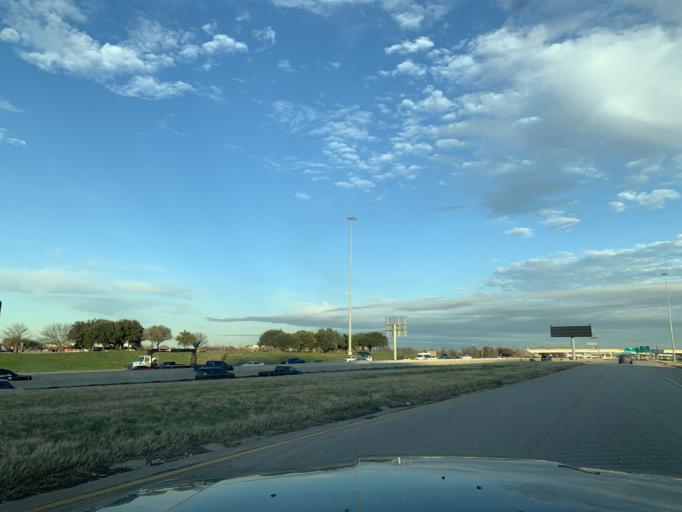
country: US
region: Texas
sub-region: Tarrant County
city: Euless
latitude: 32.8371
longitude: -97.0750
